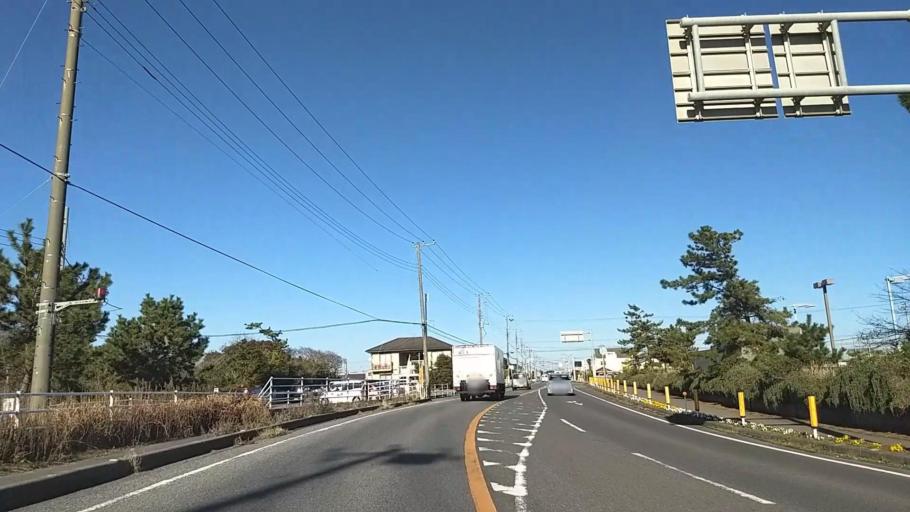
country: JP
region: Chiba
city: Togane
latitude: 35.5010
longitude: 140.4286
